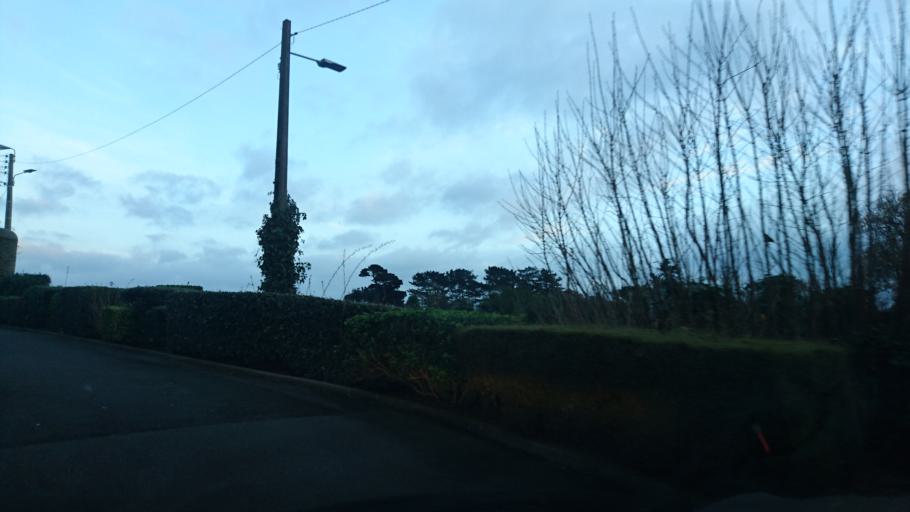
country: FR
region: Brittany
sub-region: Departement du Finistere
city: Brest
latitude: 48.3895
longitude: -4.4668
